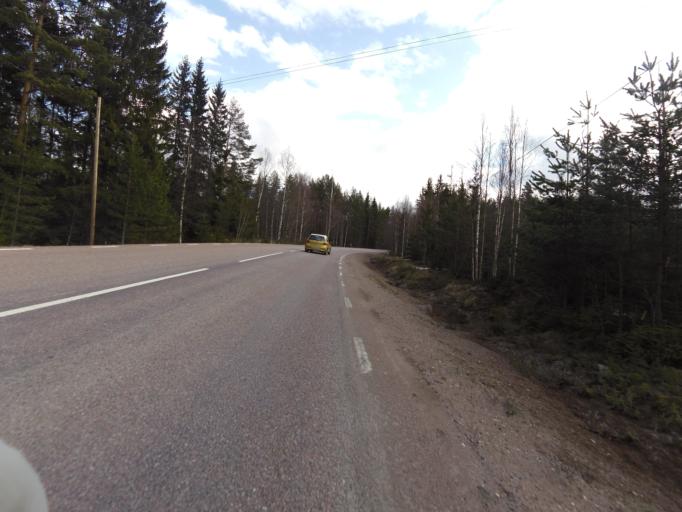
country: SE
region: Dalarna
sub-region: Avesta Kommun
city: Horndal
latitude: 60.3100
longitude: 16.2350
